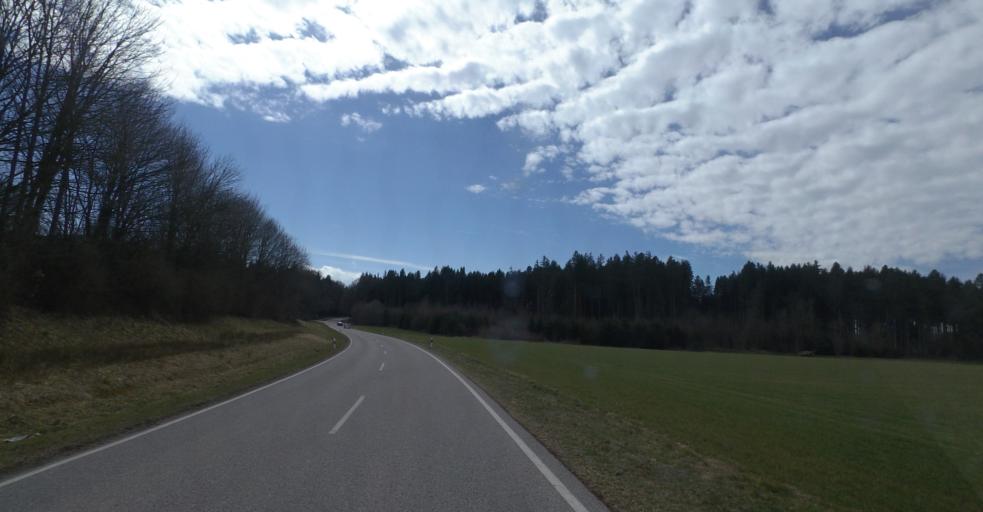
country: DE
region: Bavaria
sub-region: Upper Bavaria
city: Gstadt am Chiemsee
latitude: 47.8970
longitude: 12.4253
